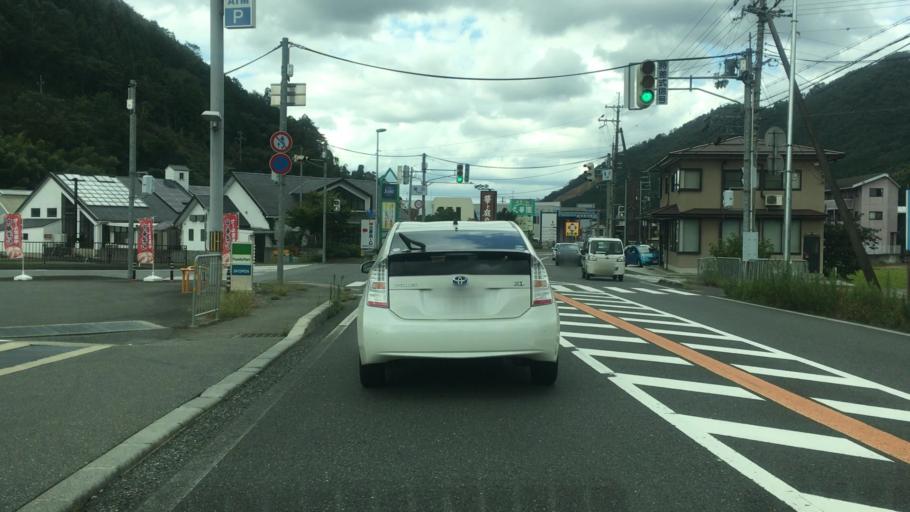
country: JP
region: Hyogo
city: Toyooka
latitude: 35.3212
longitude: 134.8794
